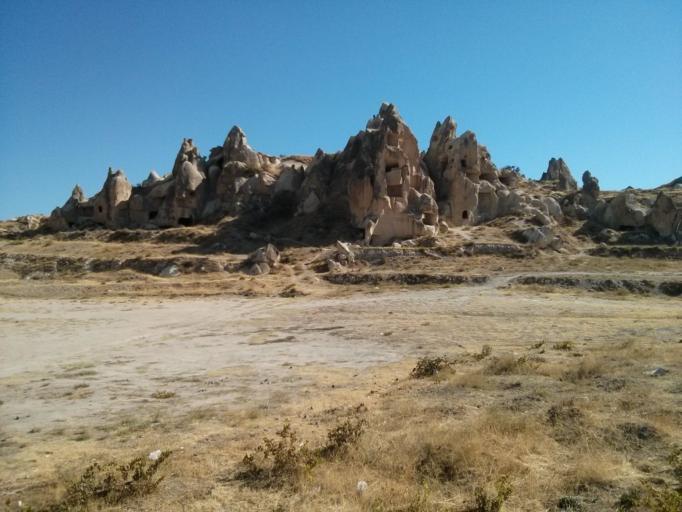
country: TR
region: Nevsehir
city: Goereme
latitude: 38.6425
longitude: 34.8423
